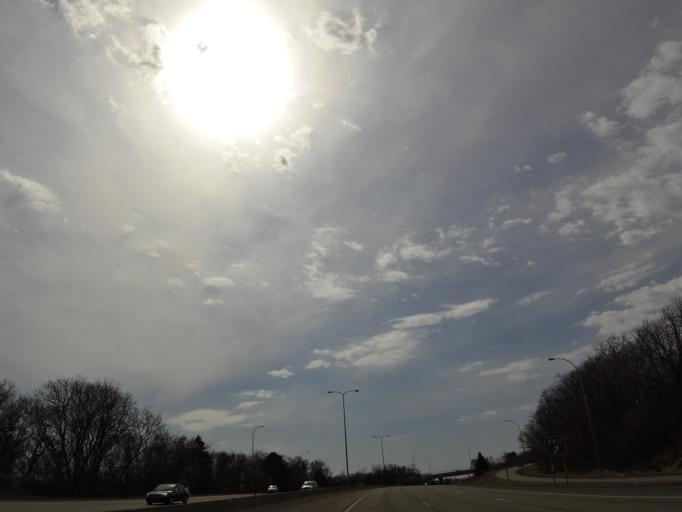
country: US
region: Minnesota
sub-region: Dakota County
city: South Saint Paul
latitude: 44.9158
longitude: -93.0636
